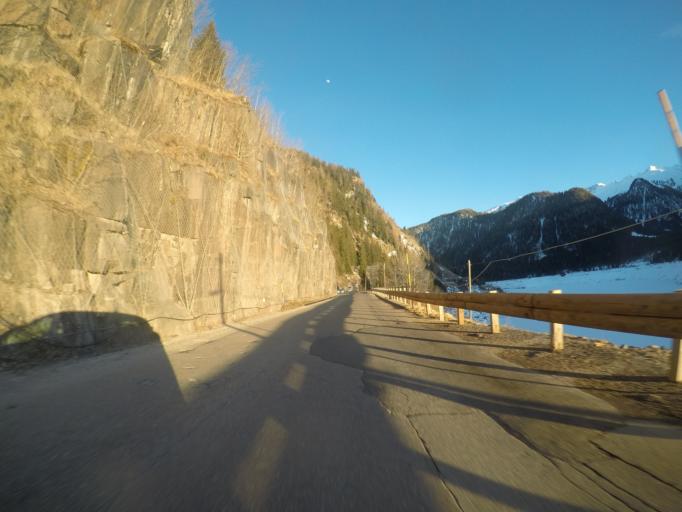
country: IT
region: Trentino-Alto Adige
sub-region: Provincia di Trento
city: Moena
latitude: 46.3059
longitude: 11.7067
